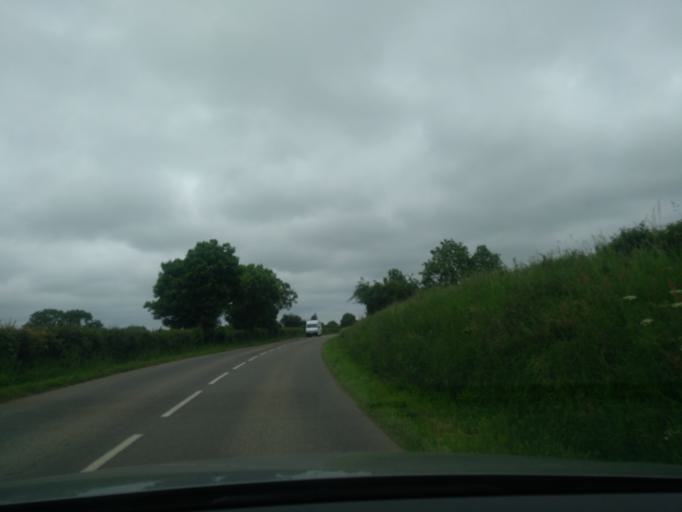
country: FR
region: Lower Normandy
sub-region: Departement de la Manche
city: Sainte-Mere-Eglise
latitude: 49.4354
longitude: -1.2954
